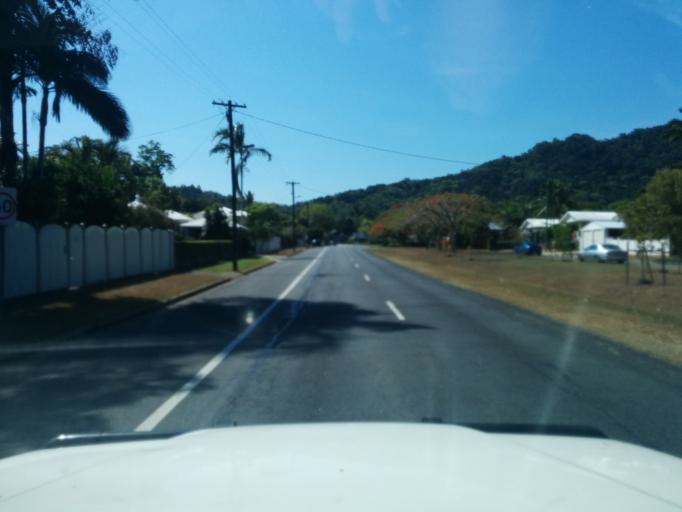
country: AU
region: Queensland
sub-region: Cairns
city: Redlynch
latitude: -16.9019
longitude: 145.7326
